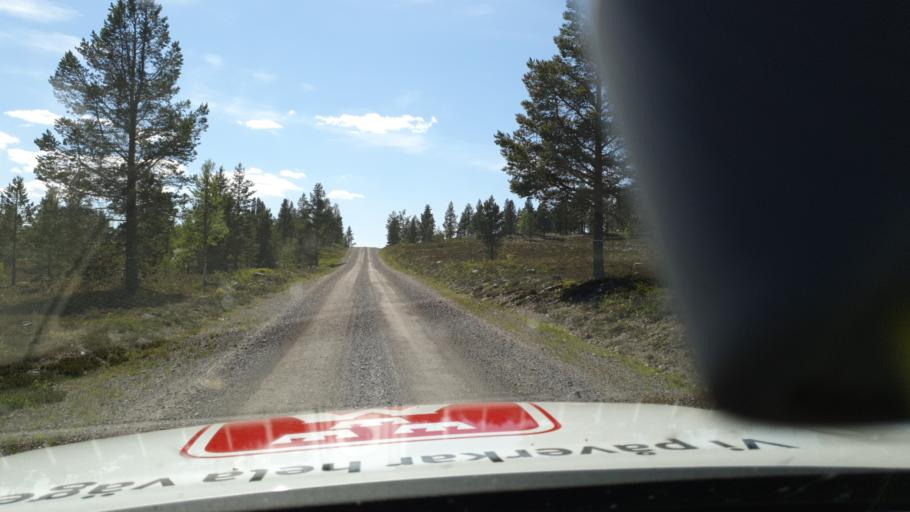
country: NO
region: Hedmark
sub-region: Engerdal
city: Engerdal
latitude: 62.1338
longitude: 12.9224
